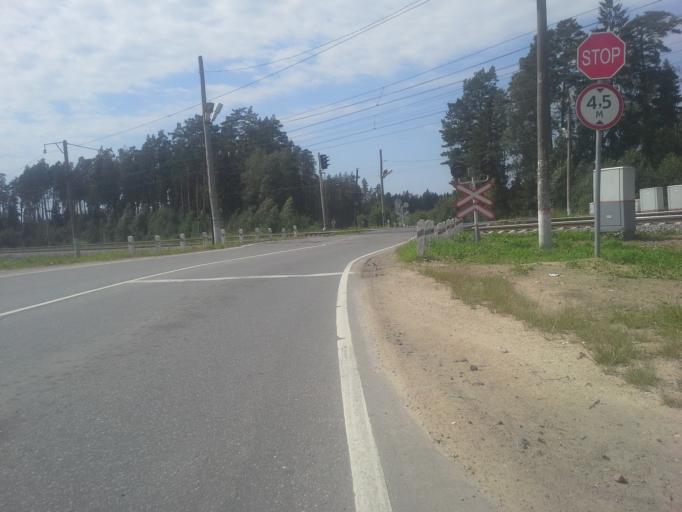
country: RU
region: Moskovskaya
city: Karinskoye
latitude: 55.6679
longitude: 36.7575
